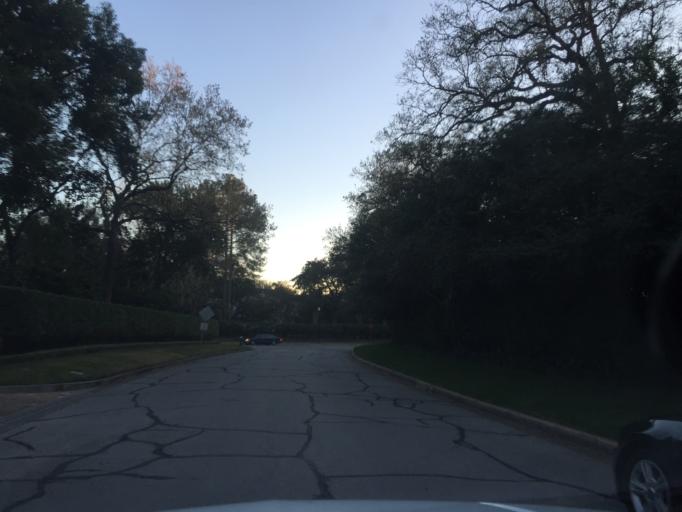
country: US
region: Texas
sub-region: Harris County
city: West University Place
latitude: 29.7524
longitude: -95.4207
